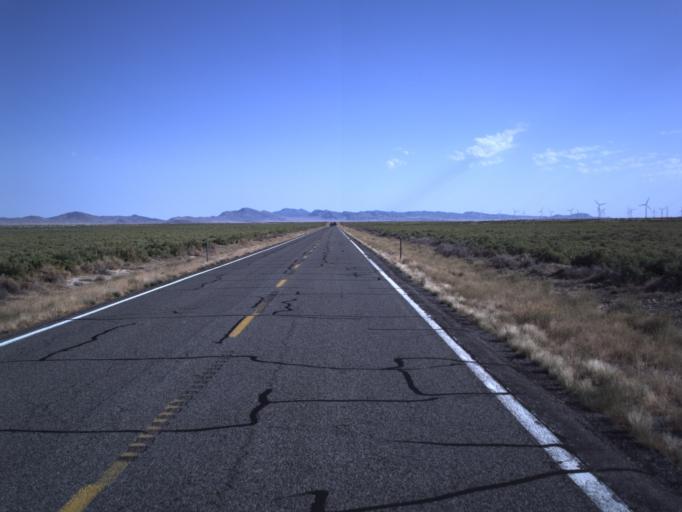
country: US
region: Utah
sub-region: Beaver County
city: Milford
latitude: 38.5145
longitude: -112.9911
